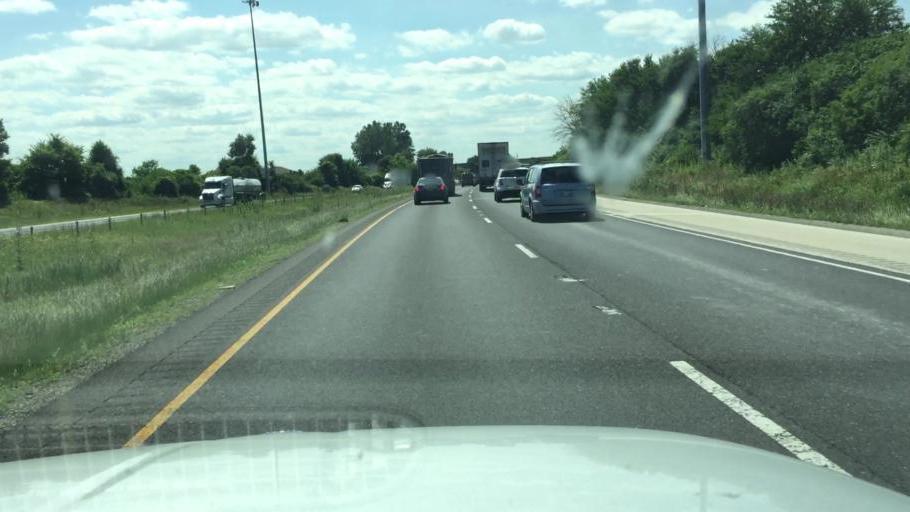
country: US
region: Illinois
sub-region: Will County
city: New Lenox
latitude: 41.5144
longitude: -87.9986
